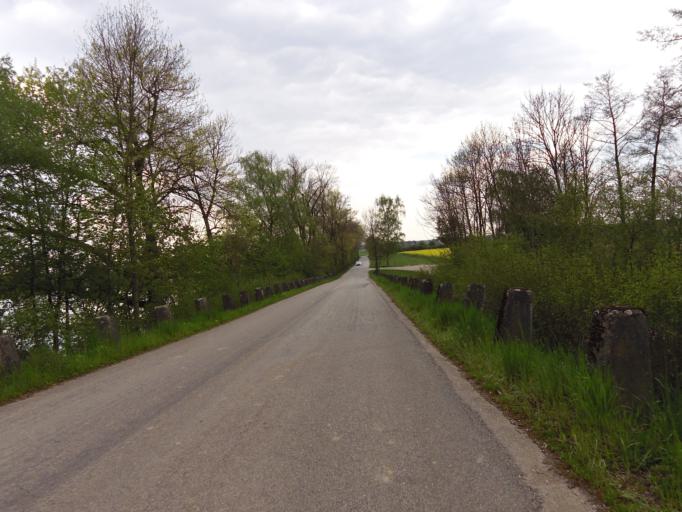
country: DE
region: Bavaria
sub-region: Upper Bavaria
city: Wartenberg
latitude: 48.4037
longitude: 11.9613
